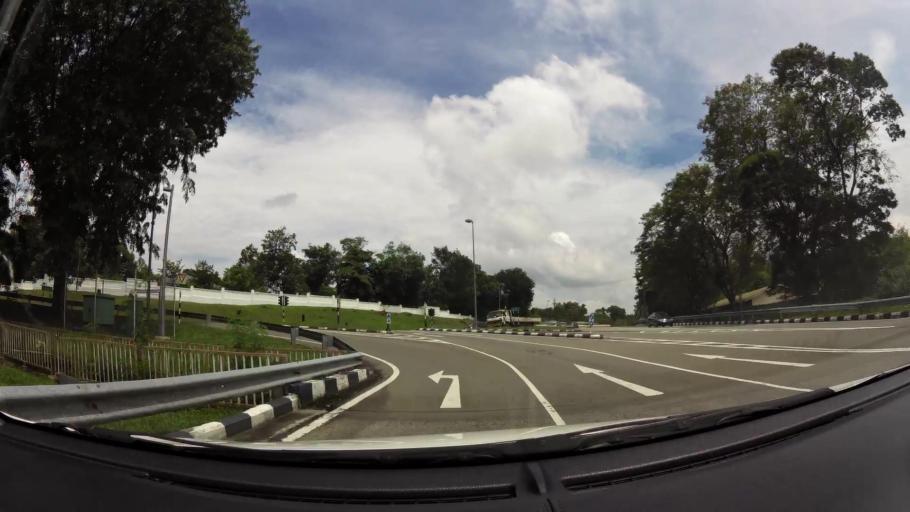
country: BN
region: Brunei and Muara
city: Bandar Seri Begawan
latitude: 4.9167
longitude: 114.9316
